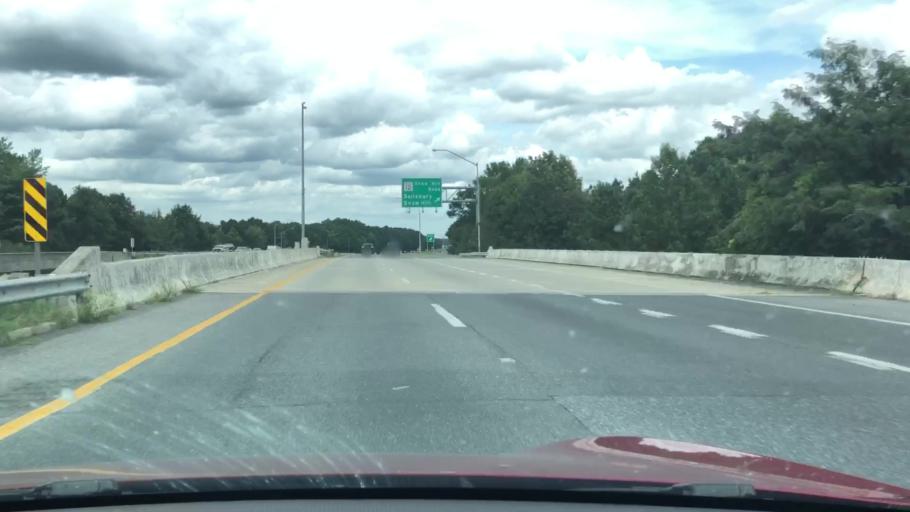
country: US
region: Maryland
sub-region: Wicomico County
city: Salisbury
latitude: 38.3328
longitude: -75.5697
